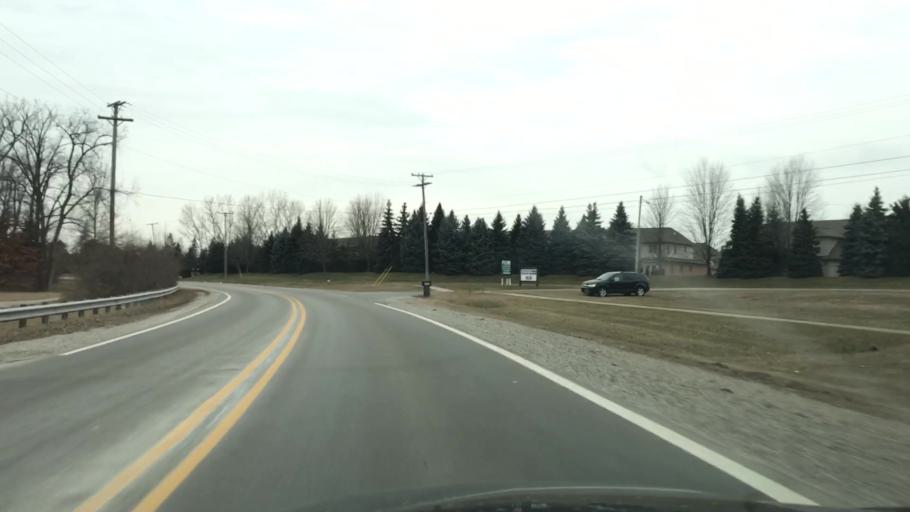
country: US
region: Michigan
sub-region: Oakland County
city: Rochester
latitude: 42.6706
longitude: -83.0846
